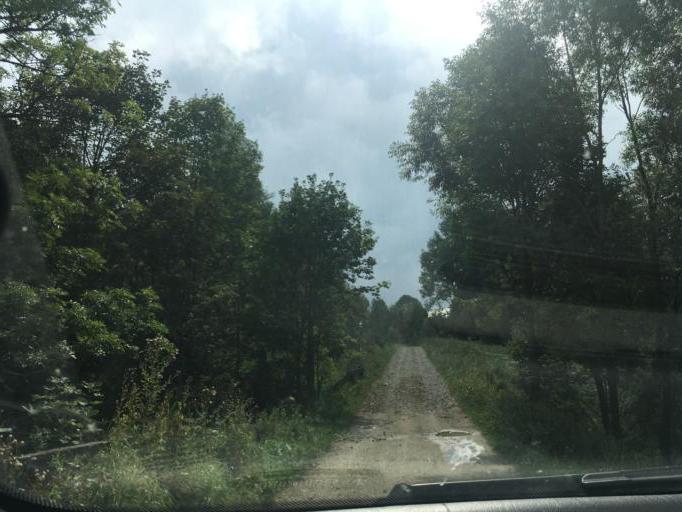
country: PL
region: Subcarpathian Voivodeship
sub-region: Powiat bieszczadzki
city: Lutowiska
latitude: 49.1617
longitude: 22.6262
